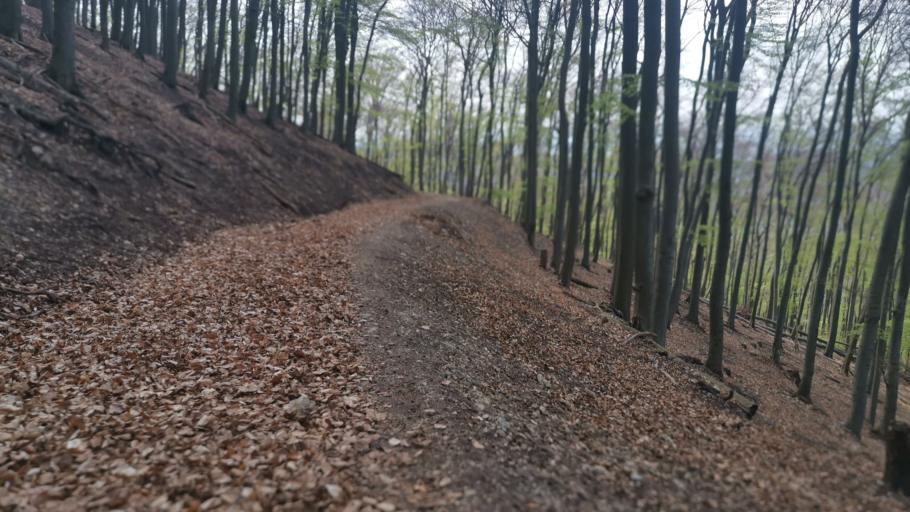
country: SK
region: Trnavsky
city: Smolenice
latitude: 48.5252
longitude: 17.3788
